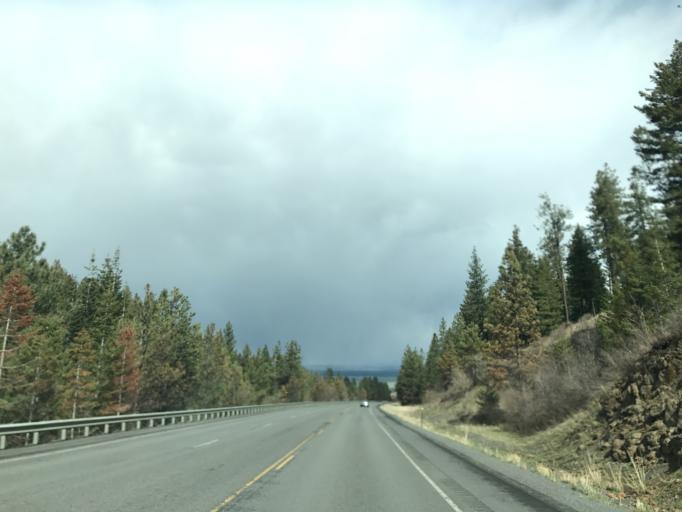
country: US
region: Idaho
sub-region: Idaho County
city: Grangeville
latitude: 45.8607
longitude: -116.2371
